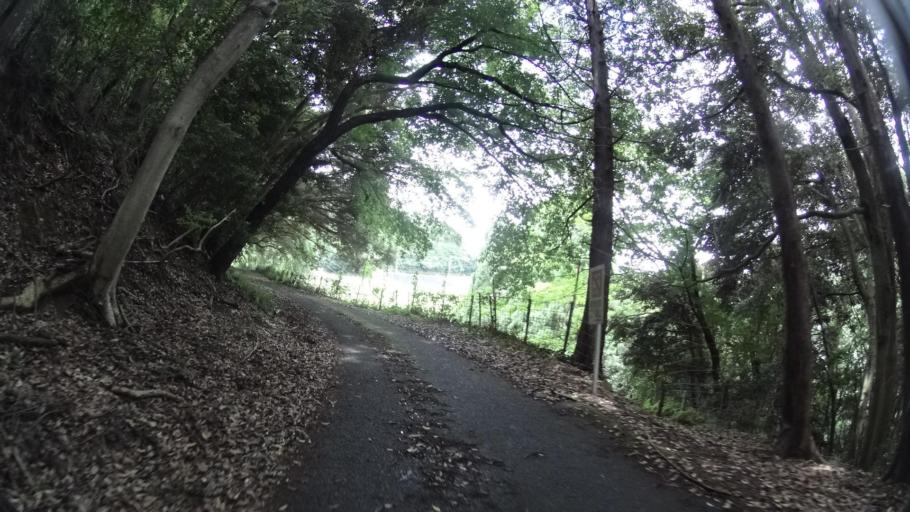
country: JP
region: Kyoto
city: Maizuru
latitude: 35.5303
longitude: 135.3415
